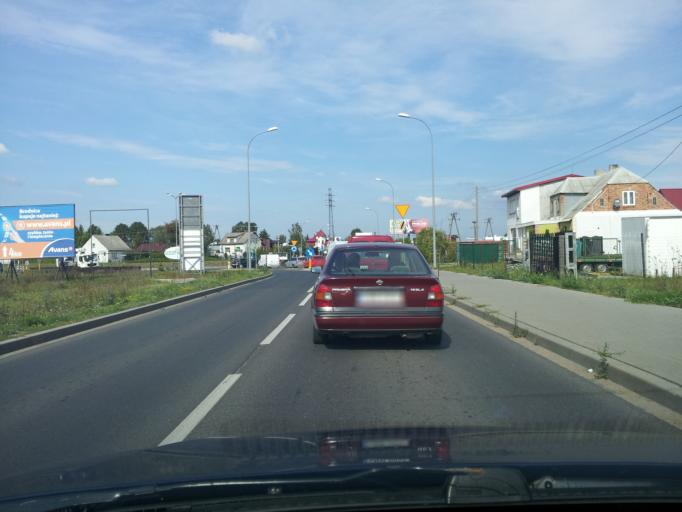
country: PL
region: Kujawsko-Pomorskie
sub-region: Powiat brodnicki
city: Brodnica
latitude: 53.2343
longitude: 19.3905
